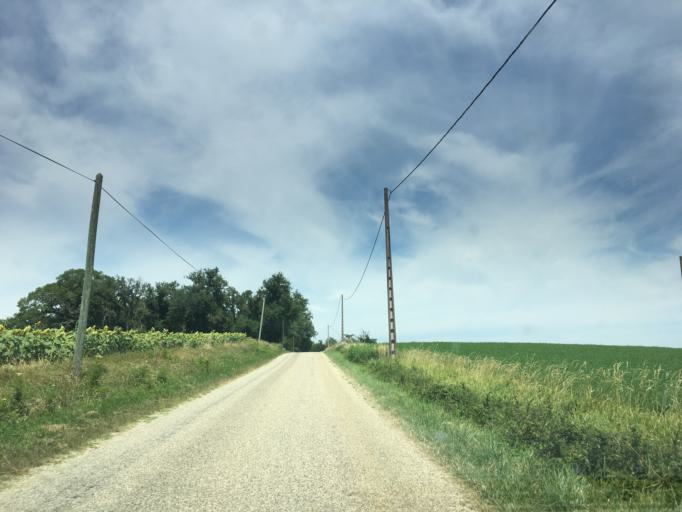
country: FR
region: Midi-Pyrenees
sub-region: Departement du Gers
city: Jegun
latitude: 43.7974
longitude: 0.4953
